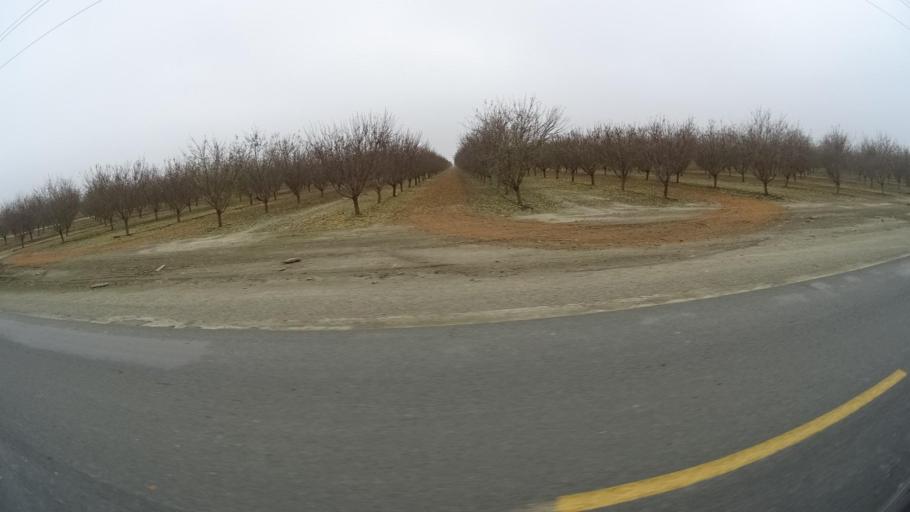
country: US
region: California
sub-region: Kern County
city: Wasco
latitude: 35.7176
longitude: -119.4111
